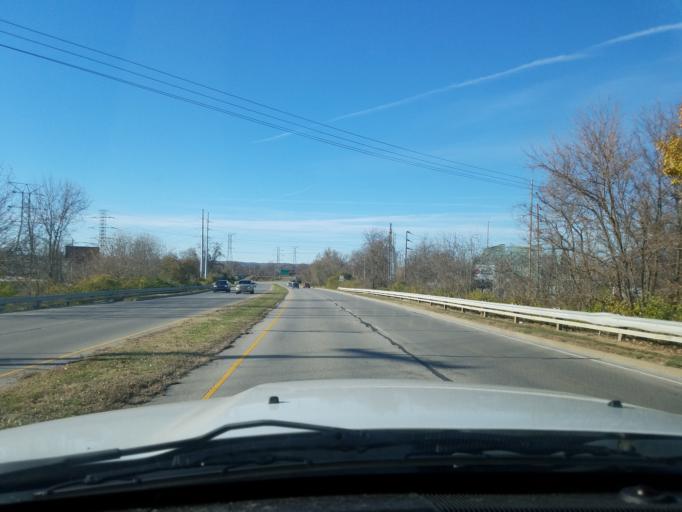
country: US
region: Indiana
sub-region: Clark County
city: Clarksville
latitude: 38.3001
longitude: -85.7765
